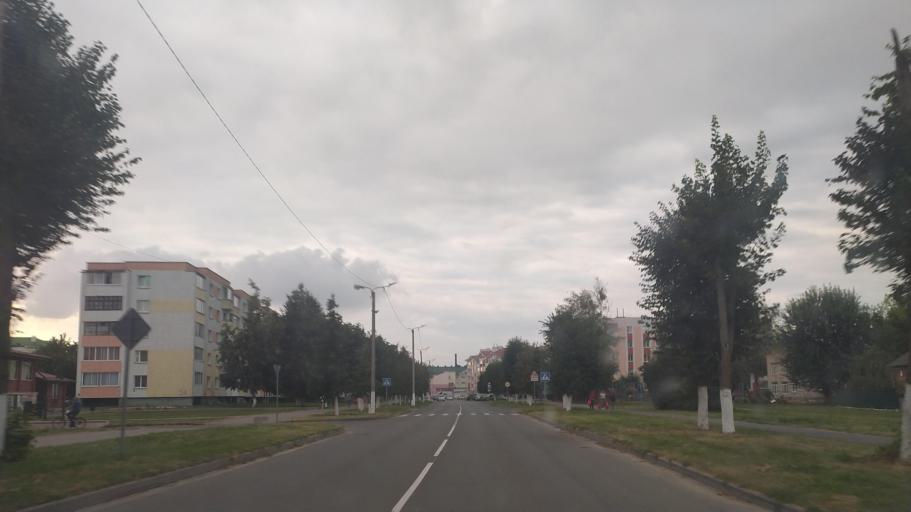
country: BY
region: Brest
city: Byaroza
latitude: 52.5312
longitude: 24.9860
